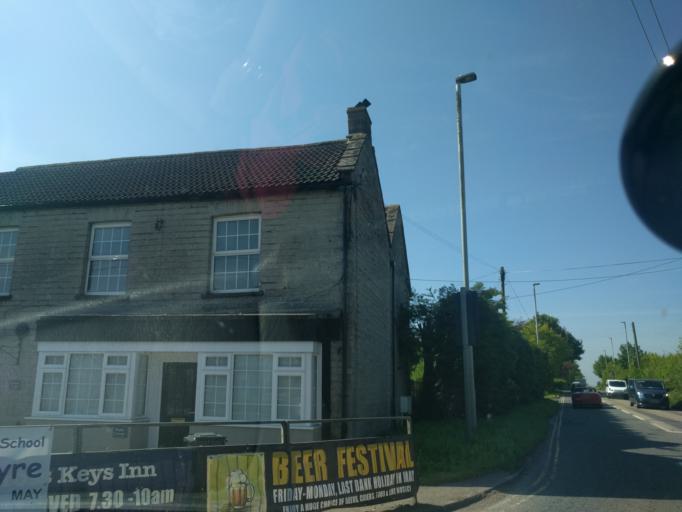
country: GB
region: England
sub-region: Somerset
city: Ilchester
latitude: 51.0758
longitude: -2.6204
